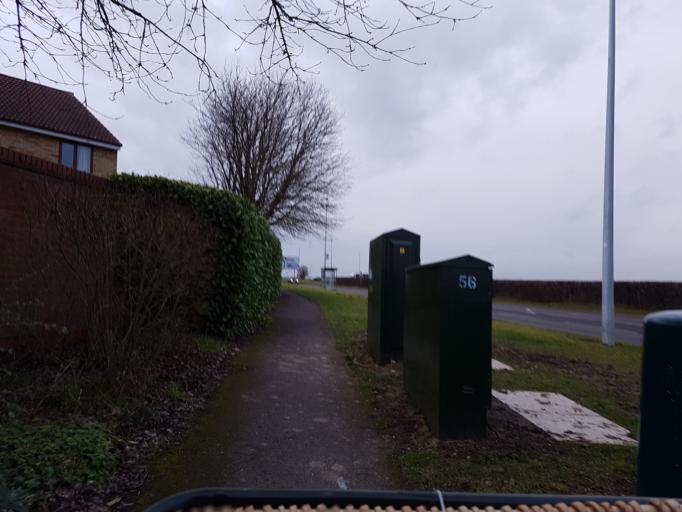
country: GB
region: England
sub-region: Cambridgeshire
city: Fulbourn
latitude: 52.1950
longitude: 0.1861
